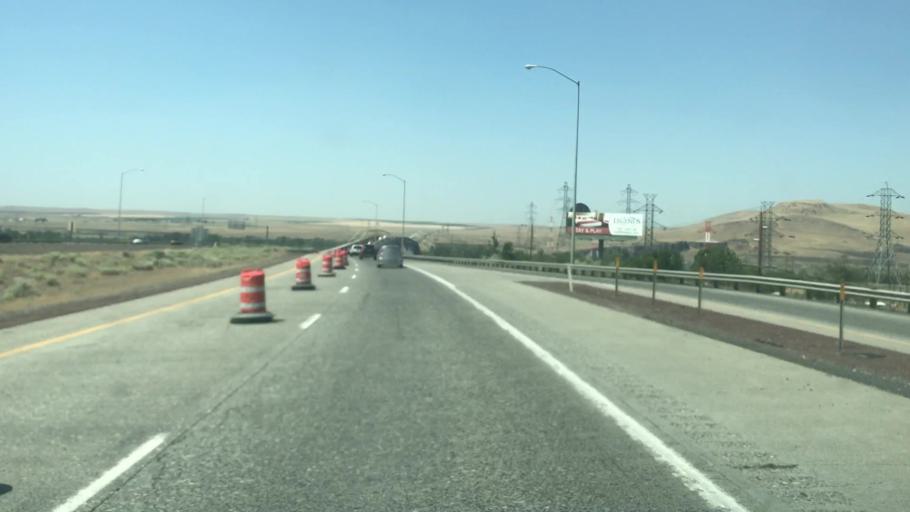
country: US
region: Oregon
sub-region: Umatilla County
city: Umatilla
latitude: 45.9198
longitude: -119.3214
